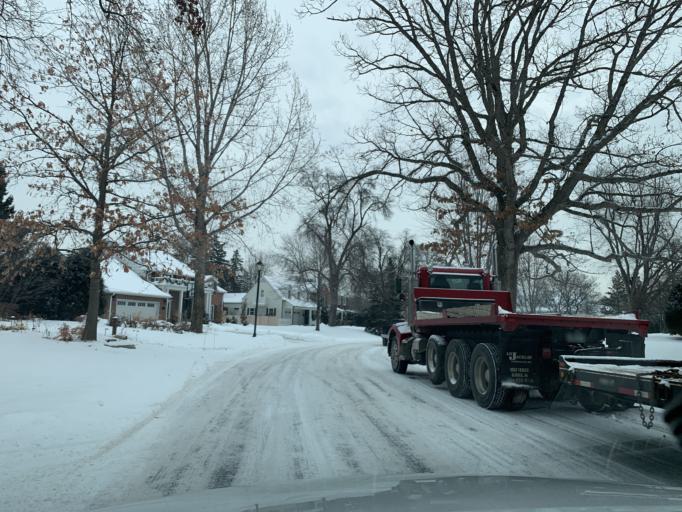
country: US
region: Minnesota
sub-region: Hennepin County
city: Edina
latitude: 44.9149
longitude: -93.3473
